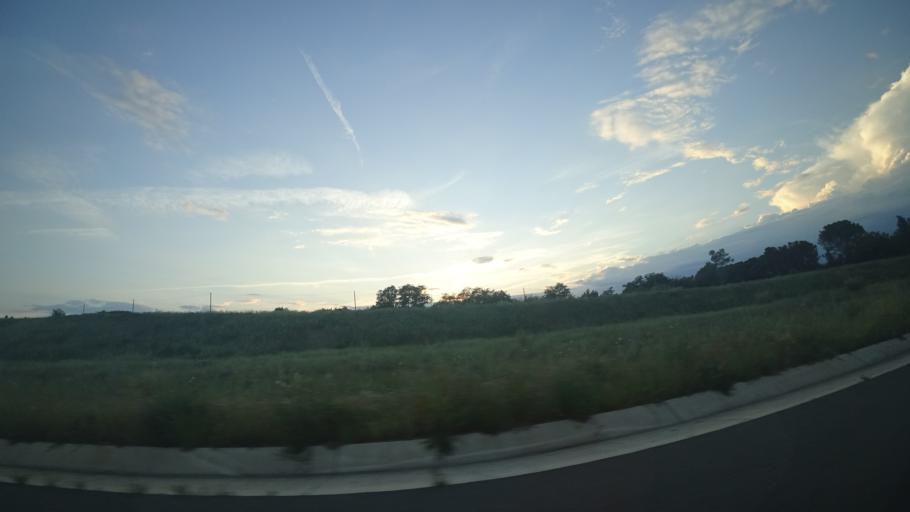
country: FR
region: Languedoc-Roussillon
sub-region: Departement de l'Herault
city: Boujan-sur-Libron
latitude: 43.3618
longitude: 3.2743
